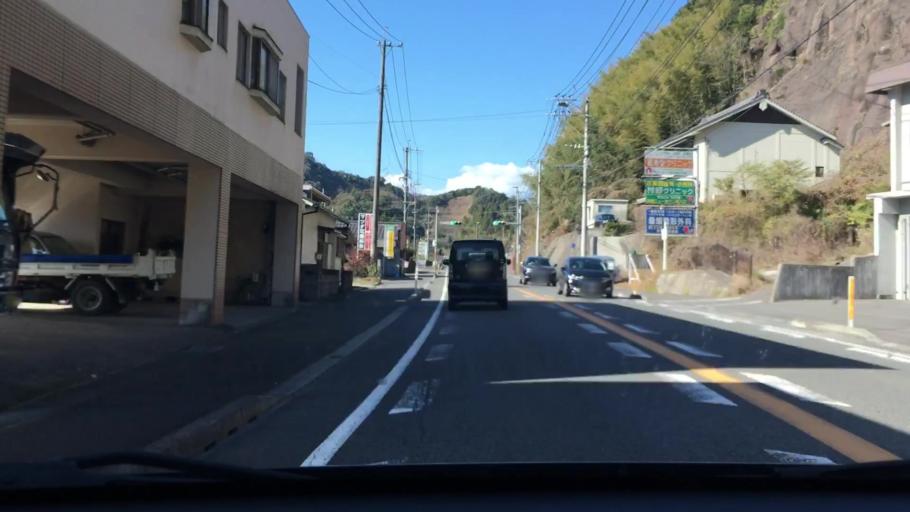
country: JP
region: Kagoshima
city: Kagoshima-shi
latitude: 31.6344
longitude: 130.5226
